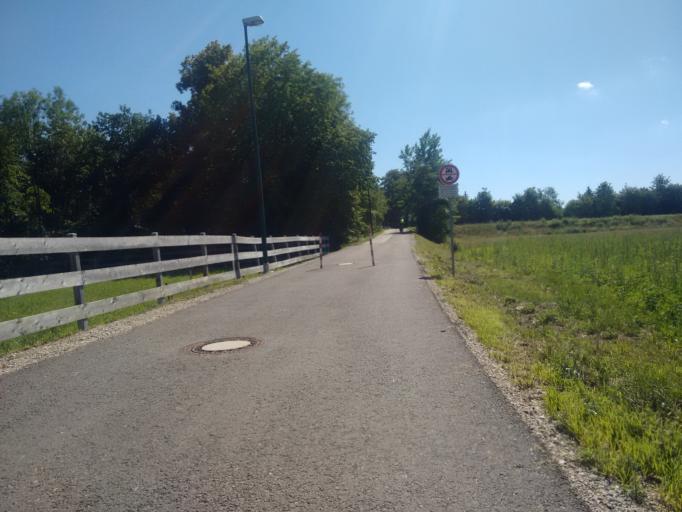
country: AT
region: Upper Austria
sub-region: Wels-Land
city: Steinhaus
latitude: 48.1419
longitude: 13.9934
